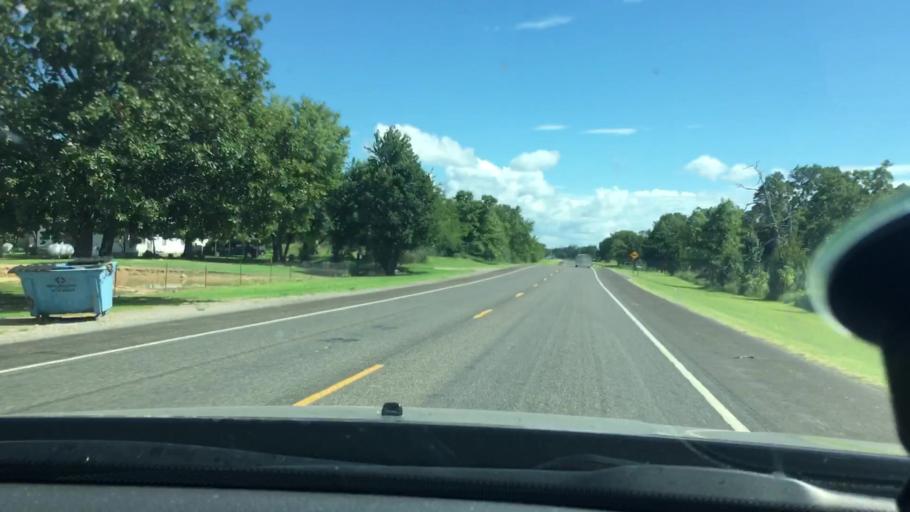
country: US
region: Oklahoma
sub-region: Sequoyah County
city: Vian
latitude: 35.5620
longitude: -94.9823
